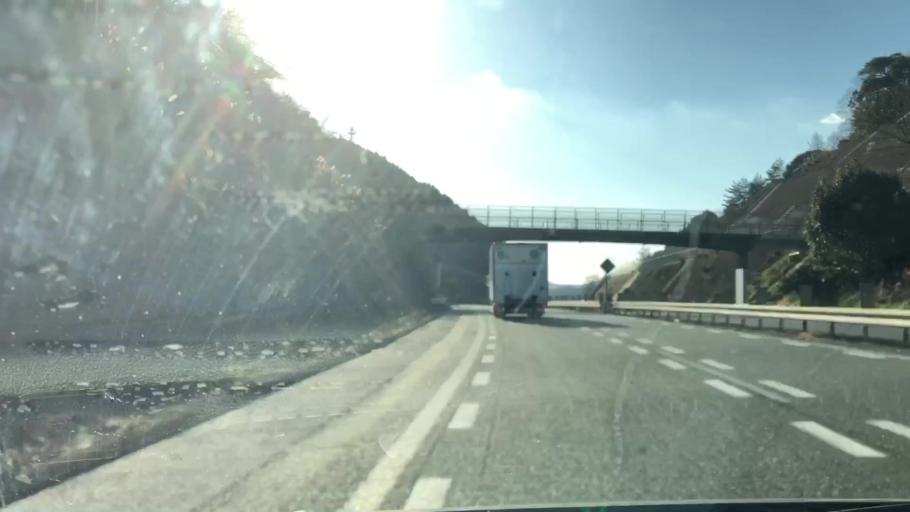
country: JP
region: Yamaguchi
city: Onoda
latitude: 34.1134
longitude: 131.1619
